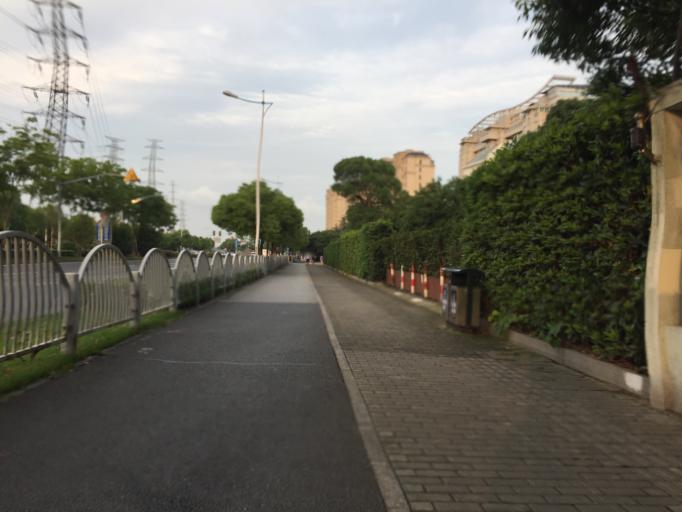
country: CN
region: Shanghai Shi
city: Huamu
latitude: 31.1896
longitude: 121.5396
